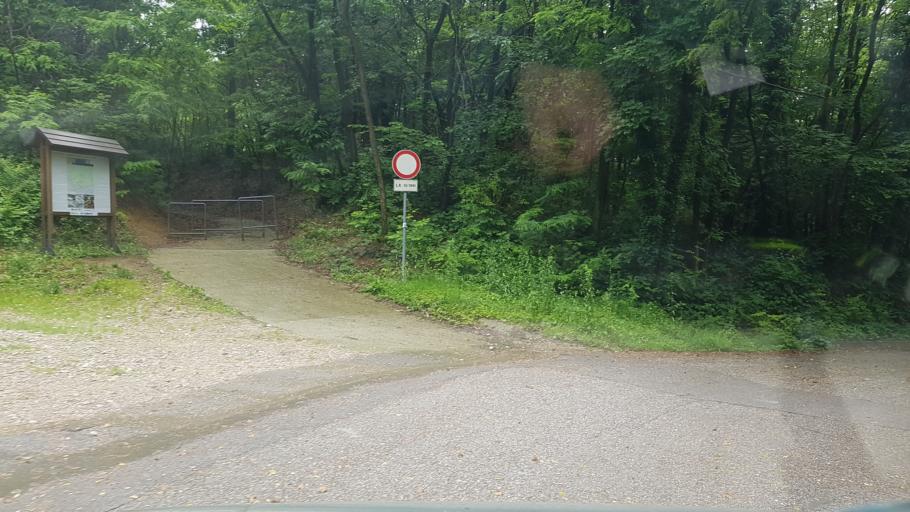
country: IT
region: Friuli Venezia Giulia
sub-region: Provincia di Gorizia
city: Gorizia
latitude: 45.9425
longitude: 13.5881
